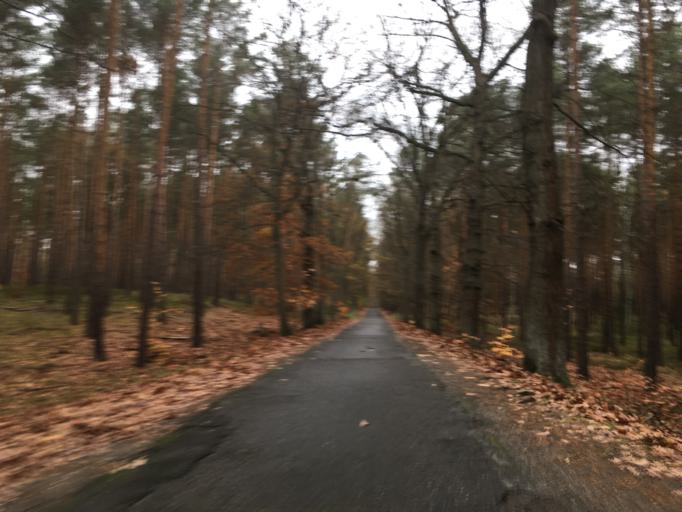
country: DE
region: Brandenburg
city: Mixdorf
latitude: 52.1706
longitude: 14.4417
